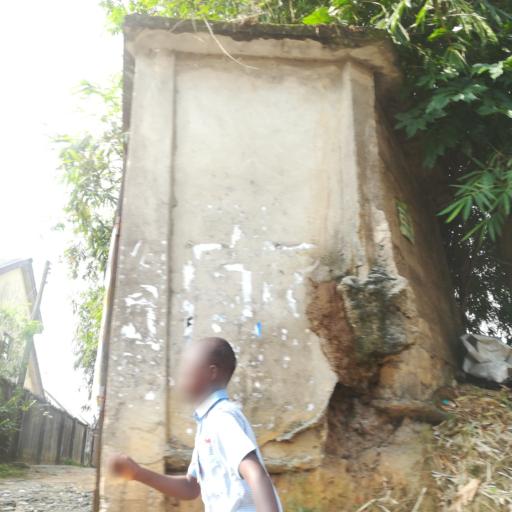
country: NG
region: Rivers
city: Port Harcourt
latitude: 4.8505
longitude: 7.0620
